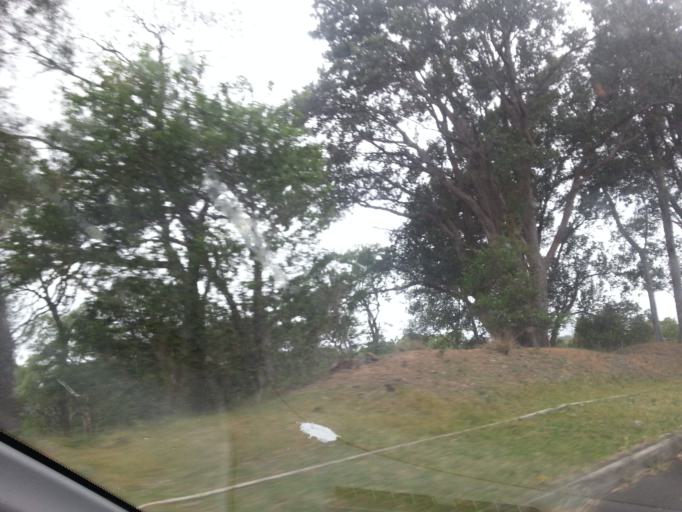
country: AU
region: New South Wales
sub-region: Wollongong
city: Keiraville
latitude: -34.4122
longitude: 150.8632
